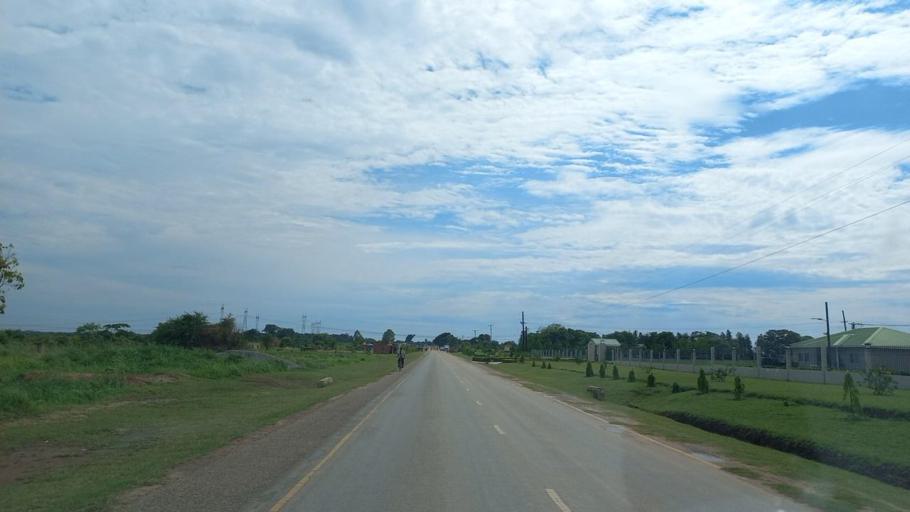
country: ZM
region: Copperbelt
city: Kitwe
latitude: -12.8723
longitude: 28.3373
